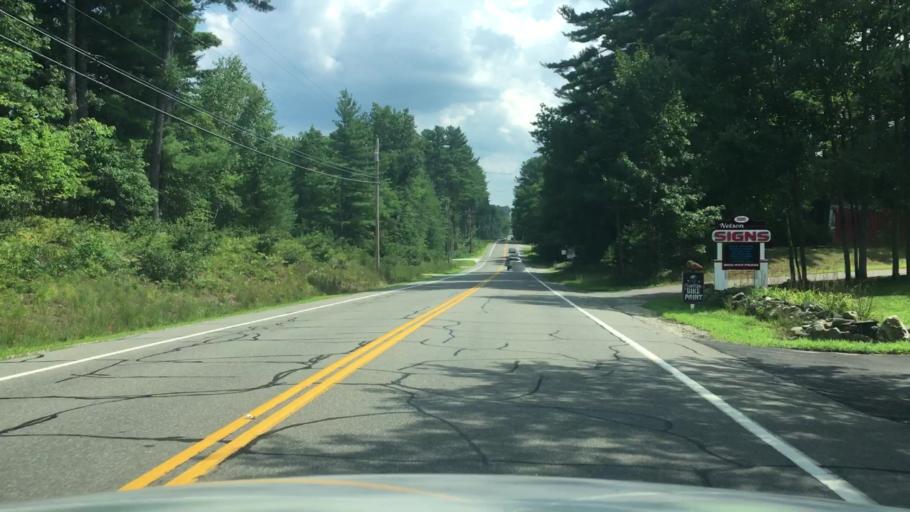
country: US
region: New Hampshire
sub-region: Rockingham County
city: Auburn
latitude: 42.9435
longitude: -71.3477
